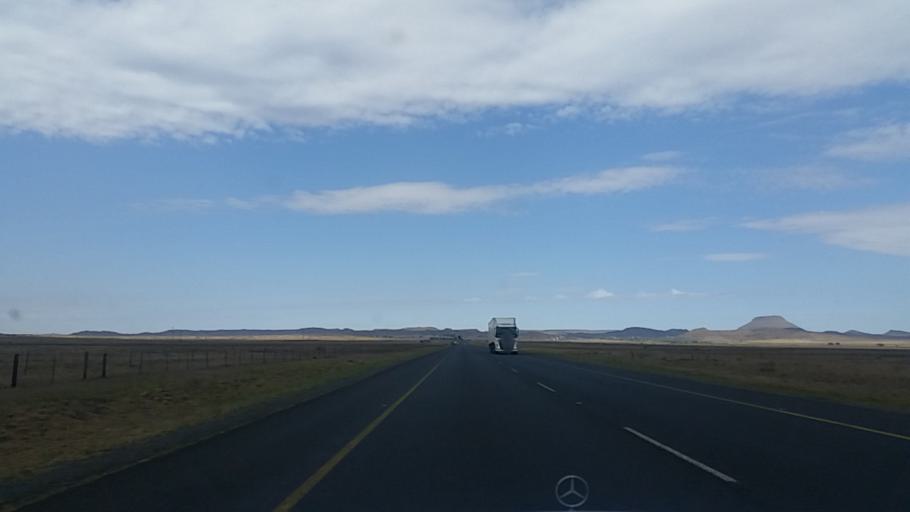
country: ZA
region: Northern Cape
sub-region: Pixley ka Seme District Municipality
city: Colesberg
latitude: -30.6777
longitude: 25.1666
